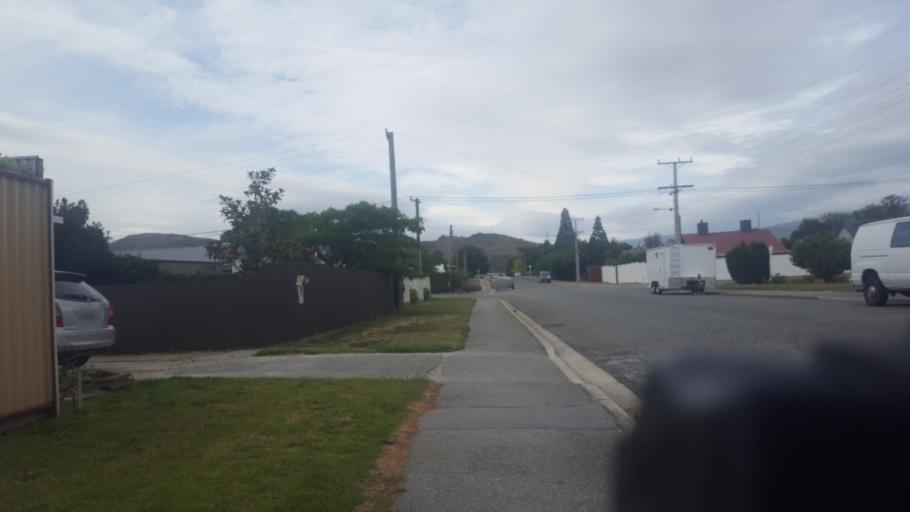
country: NZ
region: Otago
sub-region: Queenstown-Lakes District
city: Wanaka
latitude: -45.0450
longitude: 169.2111
